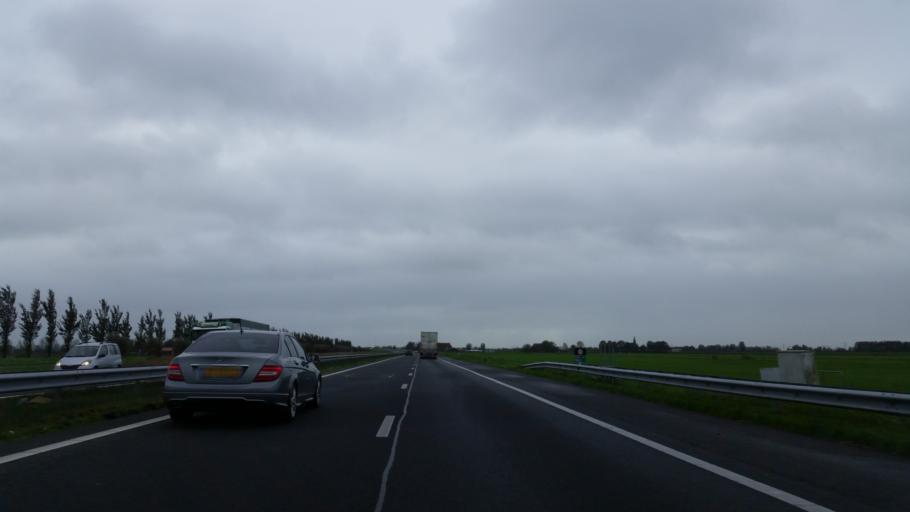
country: NL
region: Friesland
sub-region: Gemeente Boarnsterhim
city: Nes
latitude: 53.0161
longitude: 5.8687
